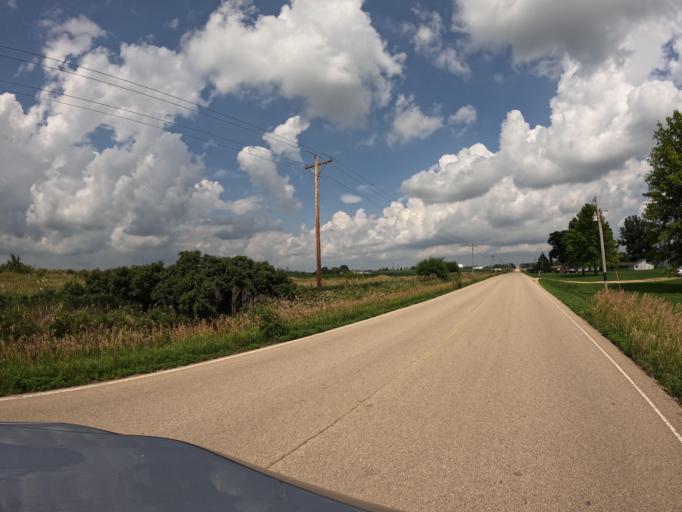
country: US
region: Iowa
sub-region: Clinton County
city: Camanche
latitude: 41.8011
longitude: -90.3218
